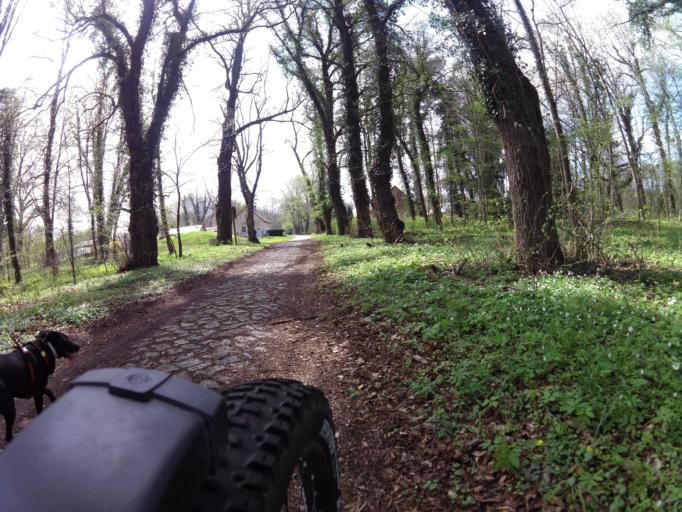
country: PL
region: West Pomeranian Voivodeship
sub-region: Powiat gryficki
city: Ploty
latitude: 53.7499
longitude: 15.3194
